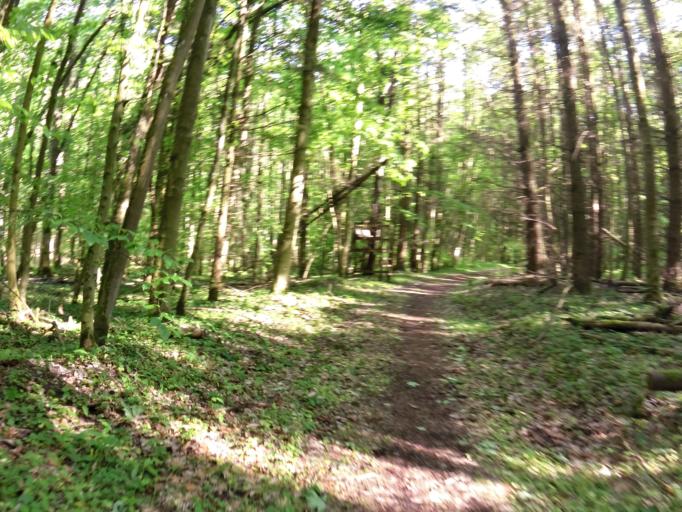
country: DE
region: Bavaria
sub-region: Regierungsbezirk Unterfranken
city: Reichenberg
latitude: 49.7412
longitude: 9.9097
